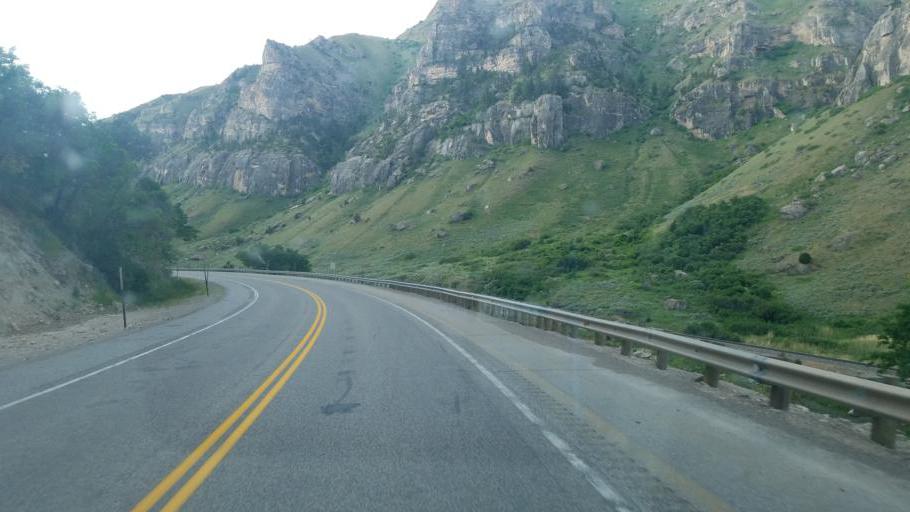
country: US
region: Wyoming
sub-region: Hot Springs County
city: Thermopolis
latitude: 43.5133
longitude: -108.1850
